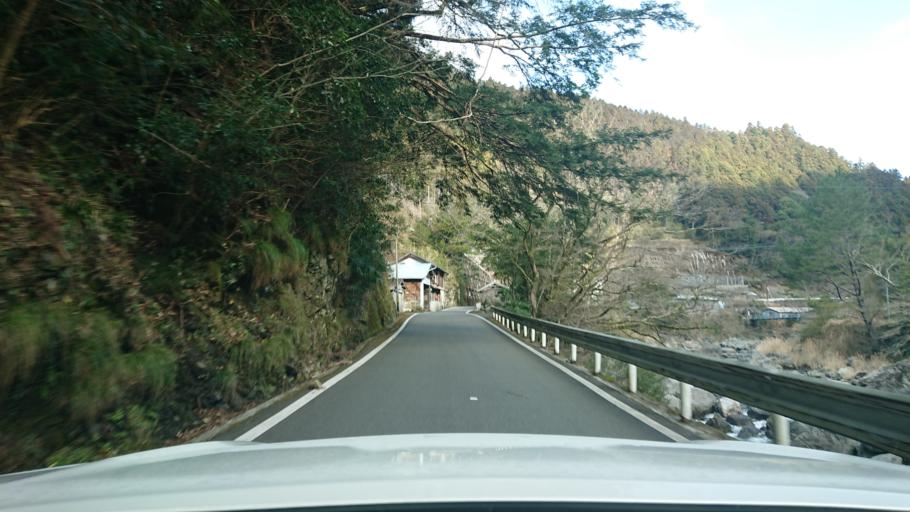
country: JP
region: Tokushima
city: Kamojimacho-jogejima
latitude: 33.9023
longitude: 134.3950
